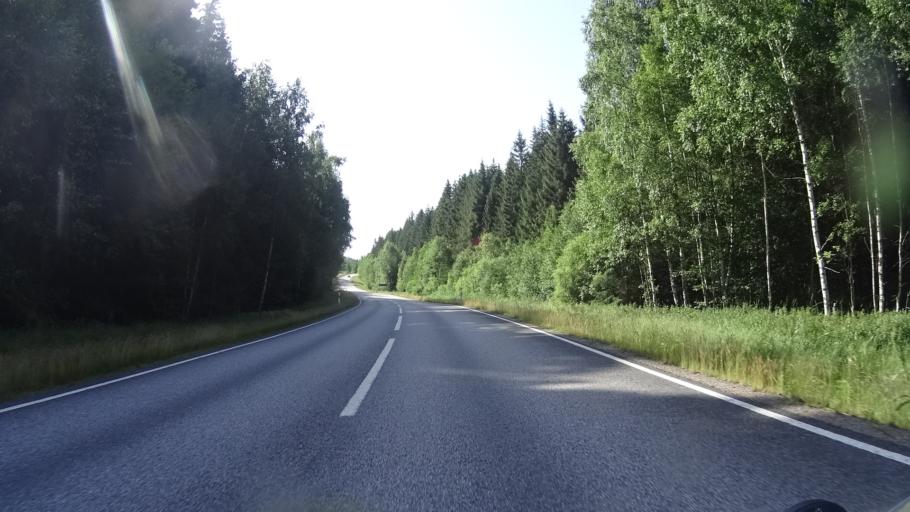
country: SE
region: Kalmar
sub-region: Vasterviks Kommun
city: Overum
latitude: 58.0521
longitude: 16.2040
